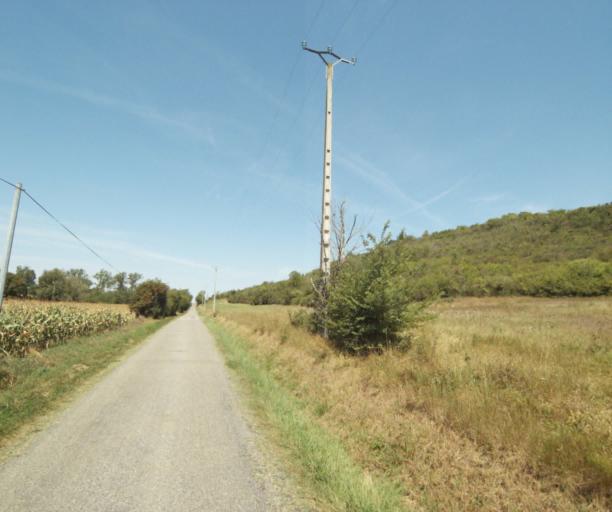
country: FR
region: Midi-Pyrenees
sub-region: Departement de la Haute-Garonne
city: Saint-Sulpice-sur-Leze
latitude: 43.3098
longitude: 1.3403
